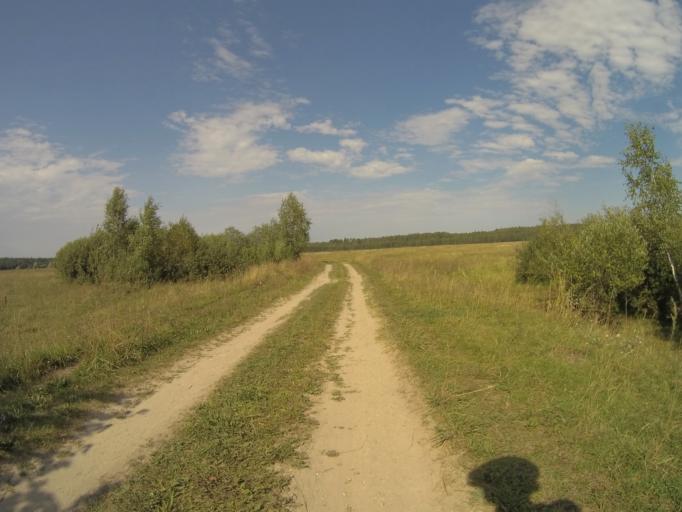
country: RU
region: Vladimir
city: Orgtrud
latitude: 56.0420
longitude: 40.6812
